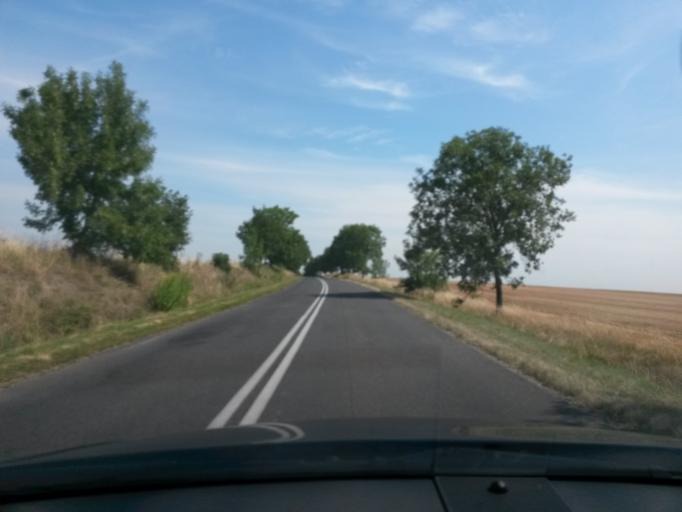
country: PL
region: Lower Silesian Voivodeship
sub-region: Powiat jaworski
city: Jawor
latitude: 51.0655
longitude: 16.2215
